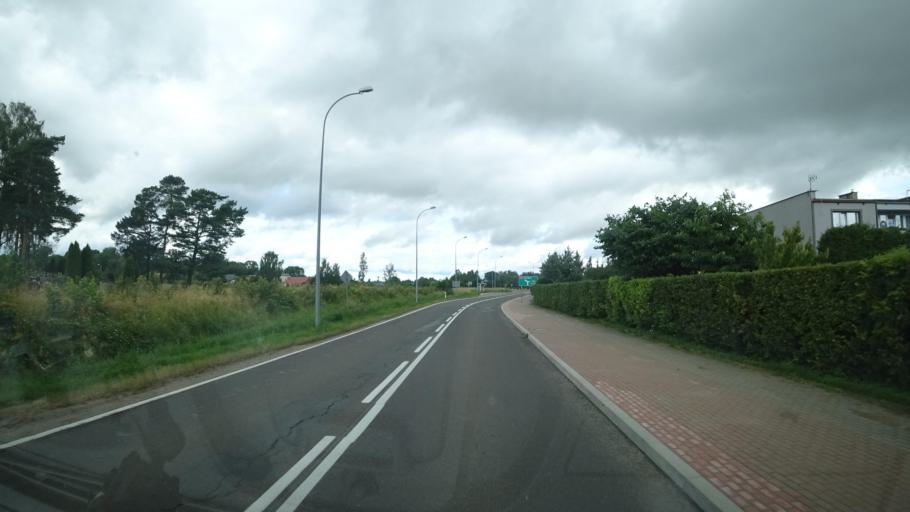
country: PL
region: Warmian-Masurian Voivodeship
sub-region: Powiat olecki
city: Kowale Oleckie
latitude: 54.1732
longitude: 22.4149
